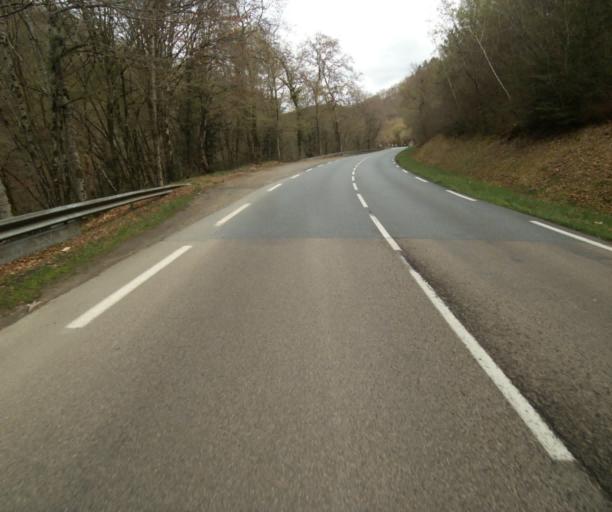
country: FR
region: Limousin
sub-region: Departement de la Correze
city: Sainte-Fortunade
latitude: 45.1882
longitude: 1.8470
